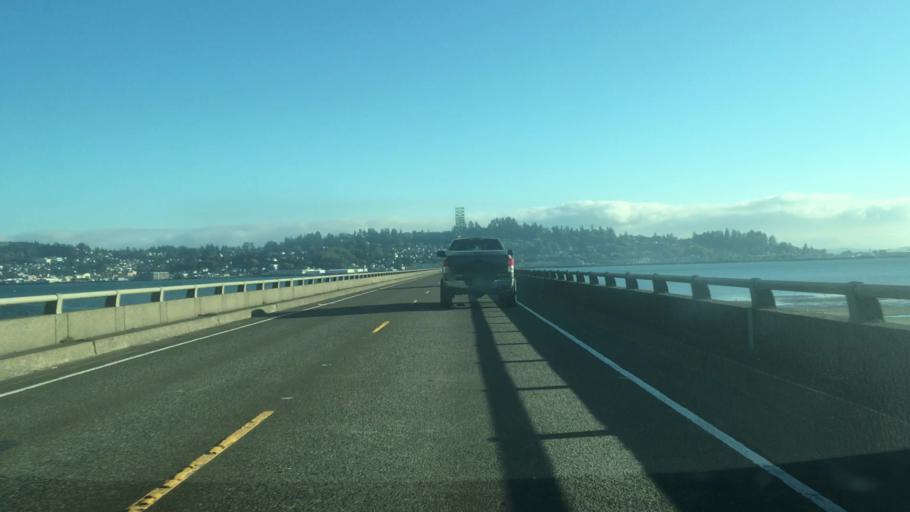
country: US
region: Oregon
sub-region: Clatsop County
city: Astoria
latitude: 46.2080
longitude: -123.8583
